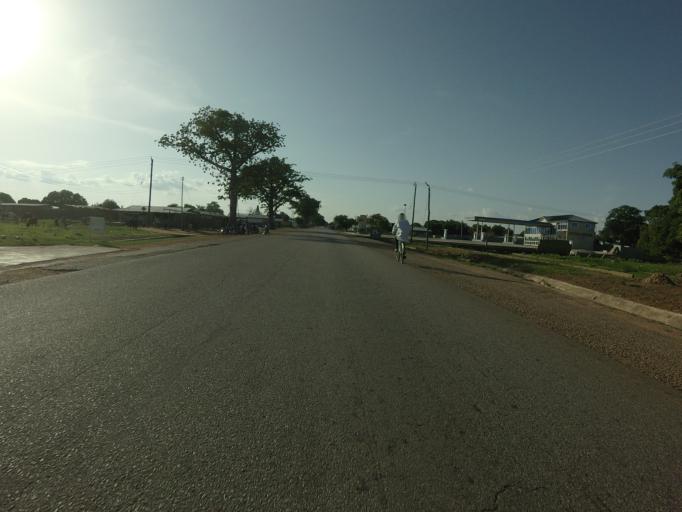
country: GH
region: Upper East
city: Navrongo
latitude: 10.9626
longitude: -1.0997
